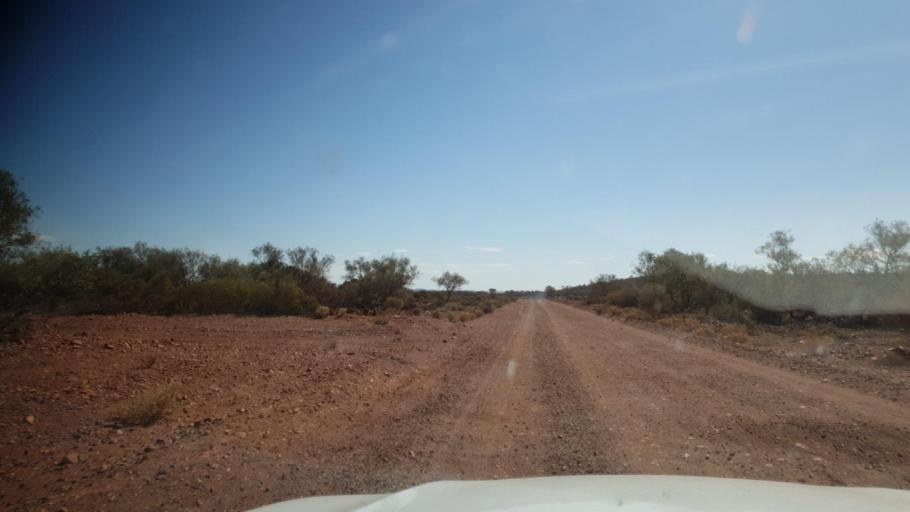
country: AU
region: South Australia
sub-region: Kimba
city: Caralue
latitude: -32.5203
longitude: 136.1306
